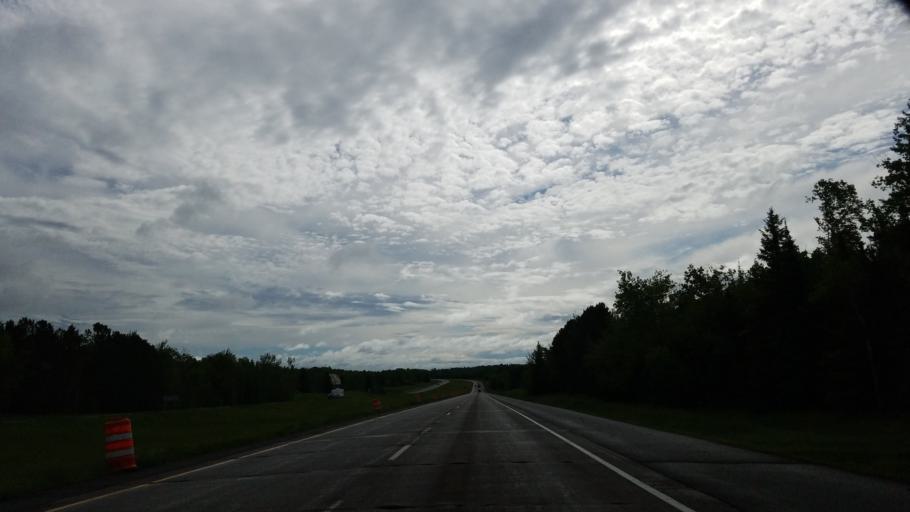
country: US
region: Minnesota
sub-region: Lake County
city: Two Harbors
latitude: 46.9285
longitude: -91.8449
